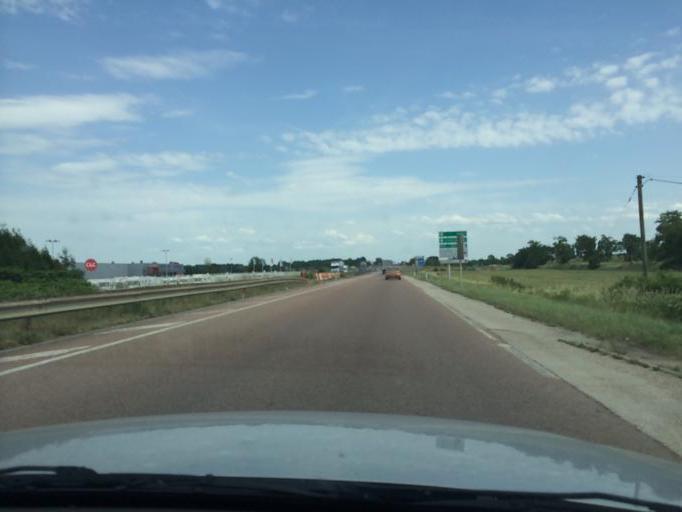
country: FR
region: Champagne-Ardenne
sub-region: Departement de la Haute-Marne
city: Villiers-en-Lieu
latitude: 48.6413
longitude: 4.9077
